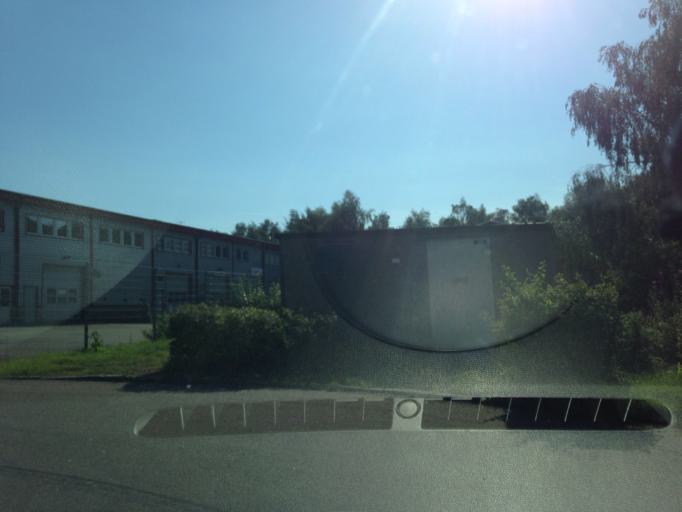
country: SE
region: Vaestra Goetaland
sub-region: Goteborg
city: Goeteborg
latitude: 57.7420
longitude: 11.9528
